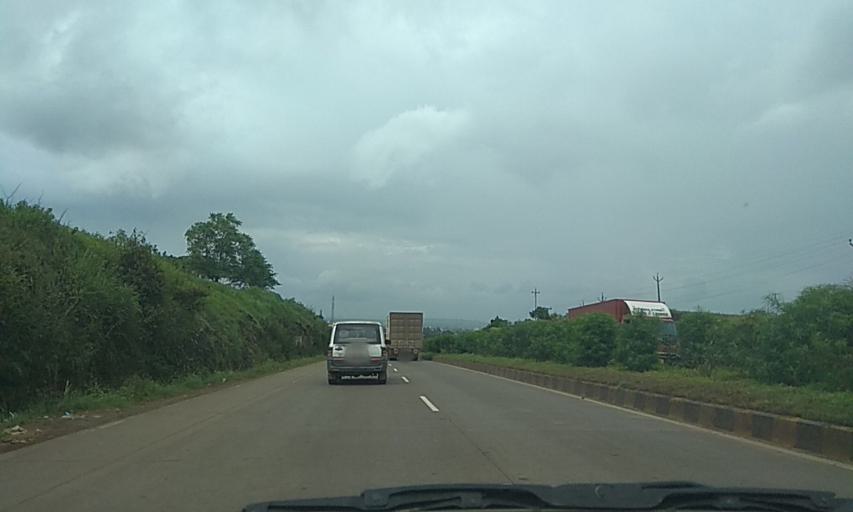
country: IN
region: Maharashtra
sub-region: Kolhapur
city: Kolhapur
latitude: 16.6762
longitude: 74.2704
